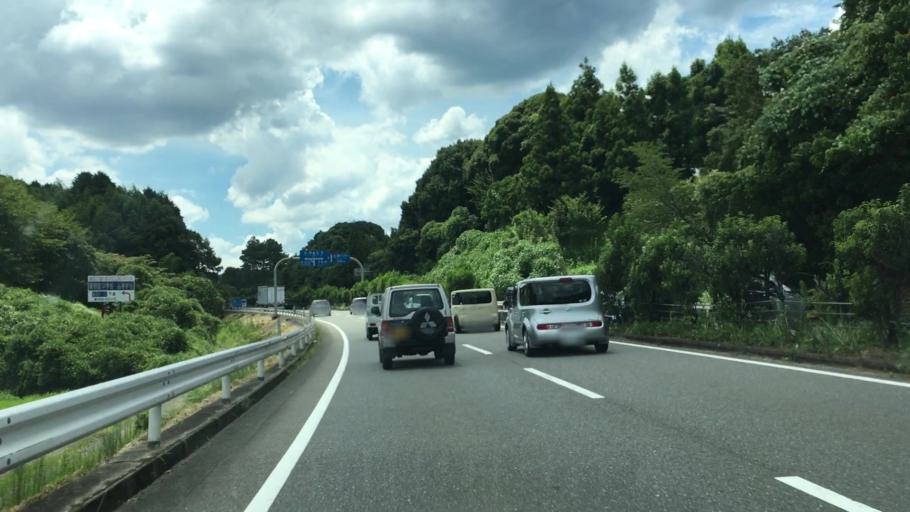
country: JP
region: Saga Prefecture
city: Tosu
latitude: 33.4308
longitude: 130.5203
